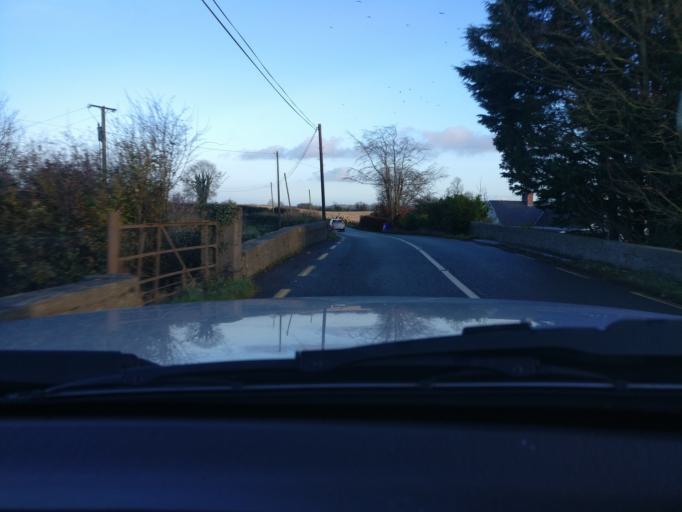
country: IE
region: Leinster
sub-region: Lu
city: Ardee
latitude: 53.8483
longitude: -6.5945
